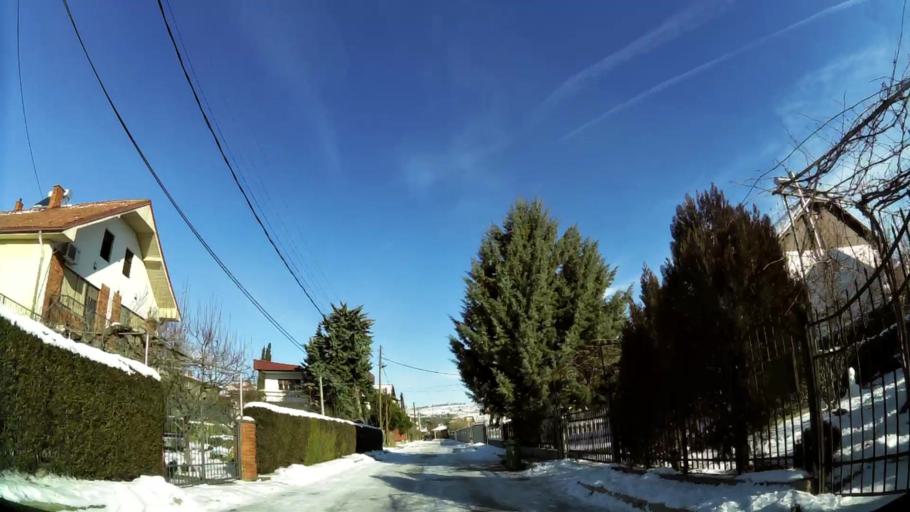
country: MK
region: Saraj
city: Saraj
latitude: 42.0052
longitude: 21.3399
